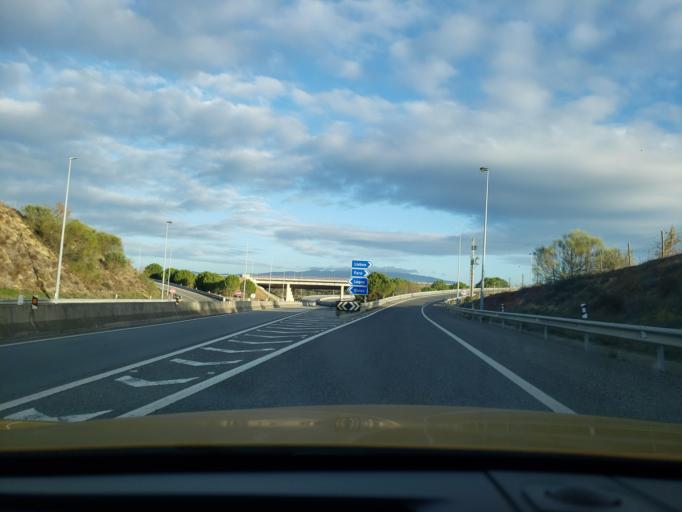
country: PT
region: Faro
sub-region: Portimao
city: Portimao
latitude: 37.1742
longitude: -8.5672
